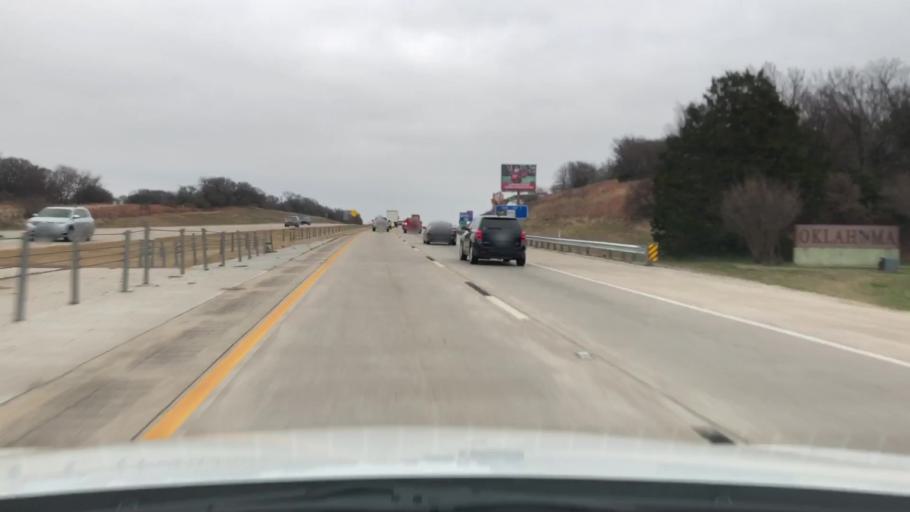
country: US
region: Texas
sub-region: Cooke County
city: Gainesville
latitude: 33.7327
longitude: -97.1538
